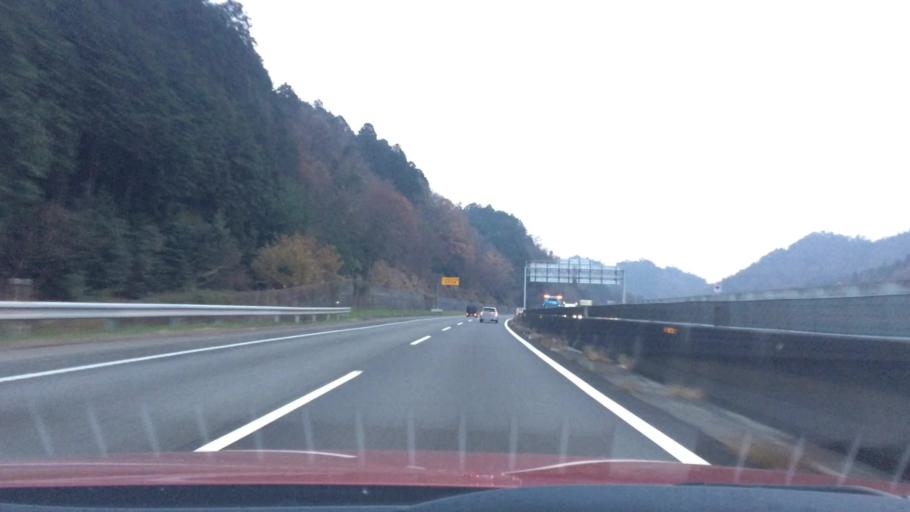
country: JP
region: Shiga Prefecture
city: Hikone
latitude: 35.3097
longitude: 136.3129
